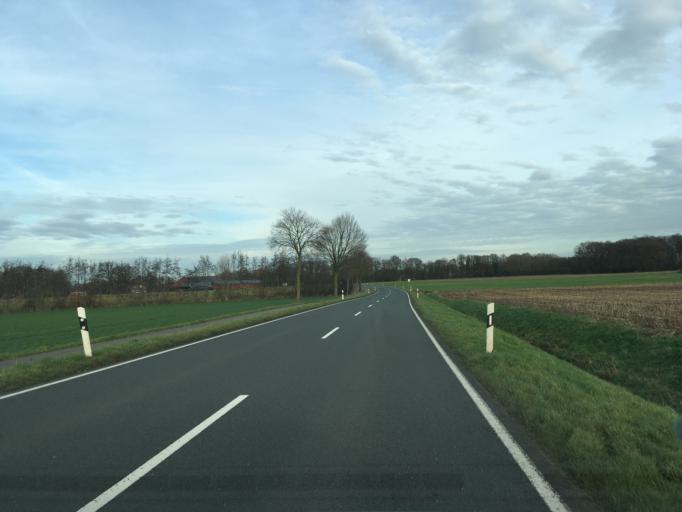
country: DE
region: North Rhine-Westphalia
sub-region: Regierungsbezirk Munster
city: Gescher
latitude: 51.9931
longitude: 7.0348
